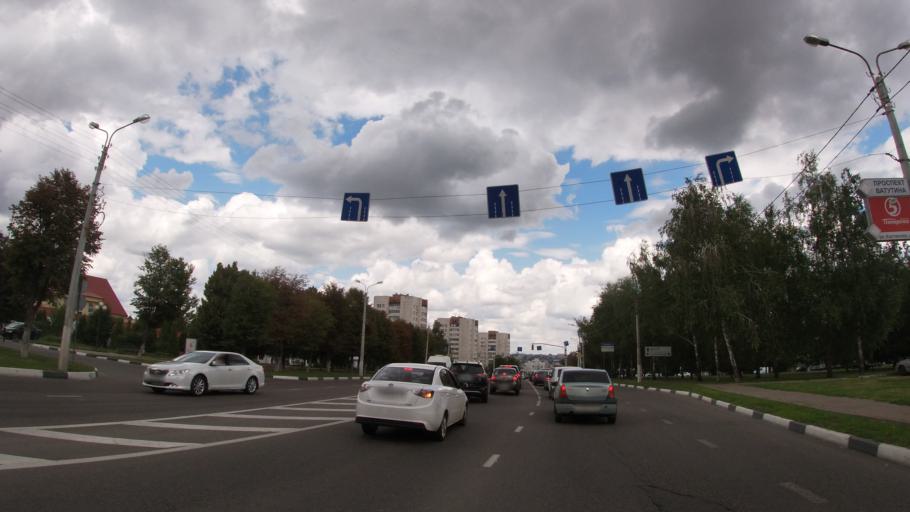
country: RU
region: Belgorod
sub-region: Belgorodskiy Rayon
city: Belgorod
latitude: 50.5775
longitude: 36.5828
